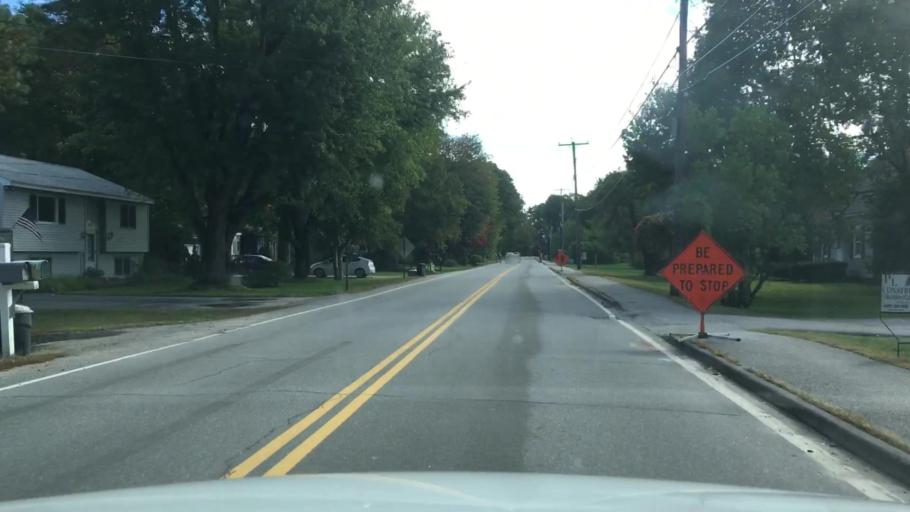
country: US
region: Maine
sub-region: Cumberland County
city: Brunswick
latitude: 43.9253
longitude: -69.9487
